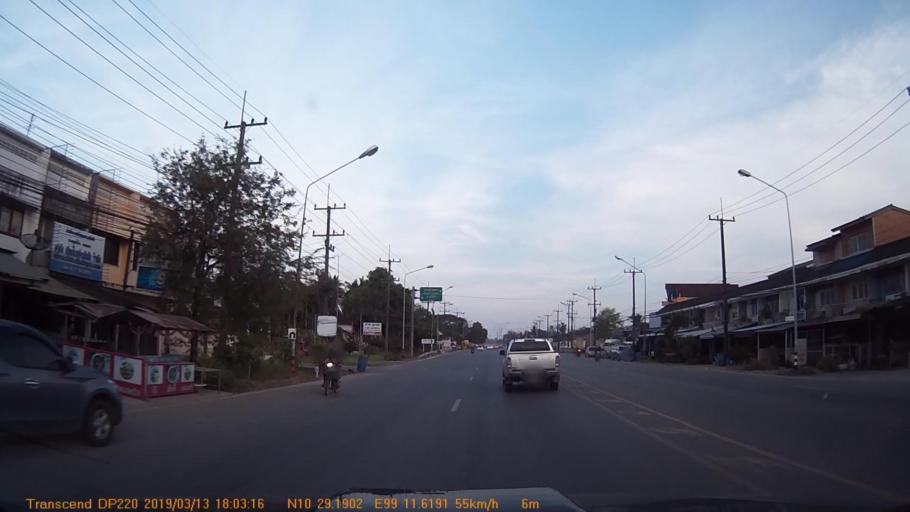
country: TH
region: Chumphon
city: Chumphon
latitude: 10.4864
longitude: 99.1938
